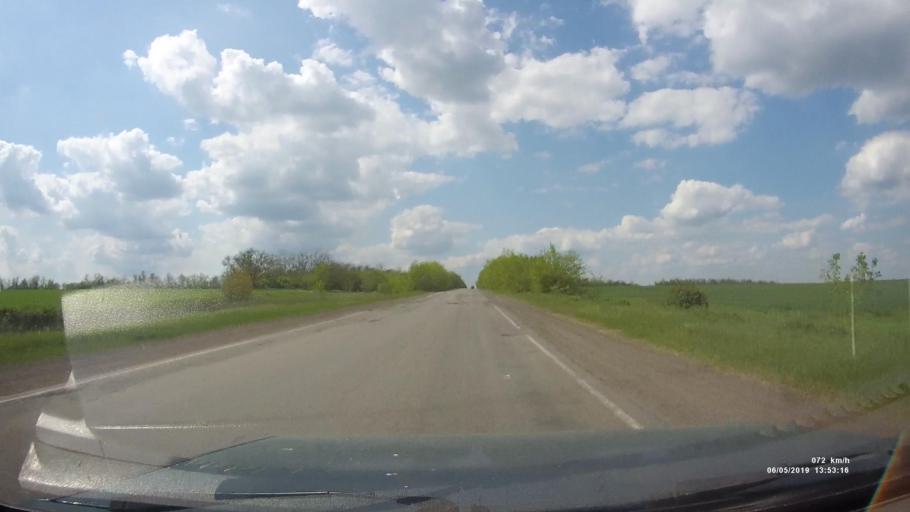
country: RU
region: Rostov
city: Melikhovskaya
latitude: 47.6673
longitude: 40.4646
